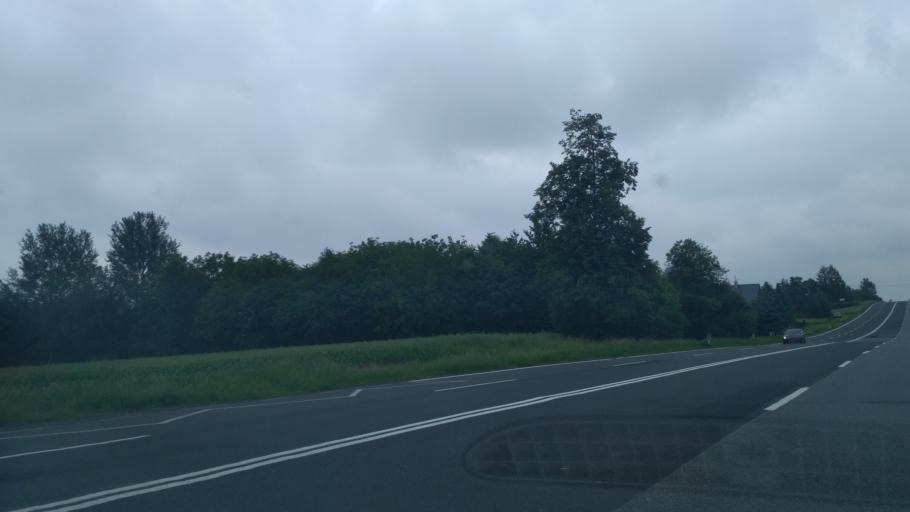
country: PL
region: Subcarpathian Voivodeship
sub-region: Powiat lancucki
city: Rogozno
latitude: 50.0670
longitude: 22.3893
